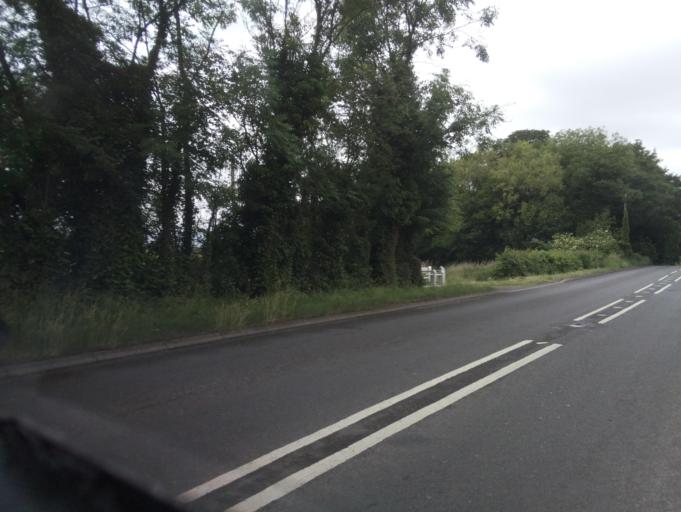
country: GB
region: England
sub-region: Staffordshire
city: Burton upon Trent
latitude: 52.8391
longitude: -1.6650
